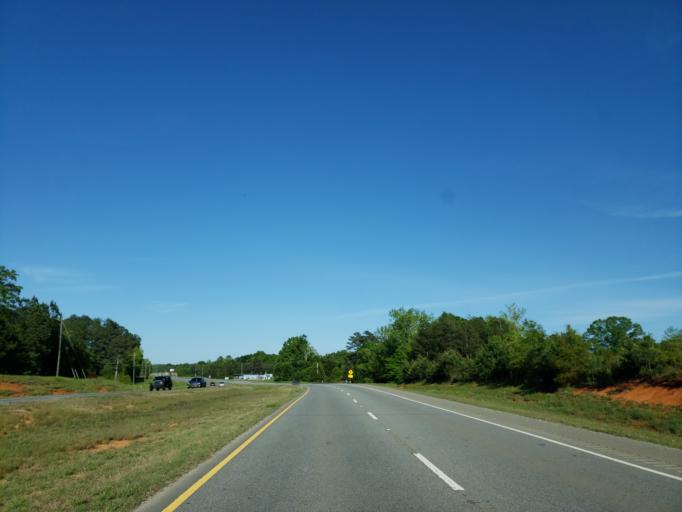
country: US
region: Georgia
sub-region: Polk County
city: Aragon
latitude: 34.0039
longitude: -85.1530
